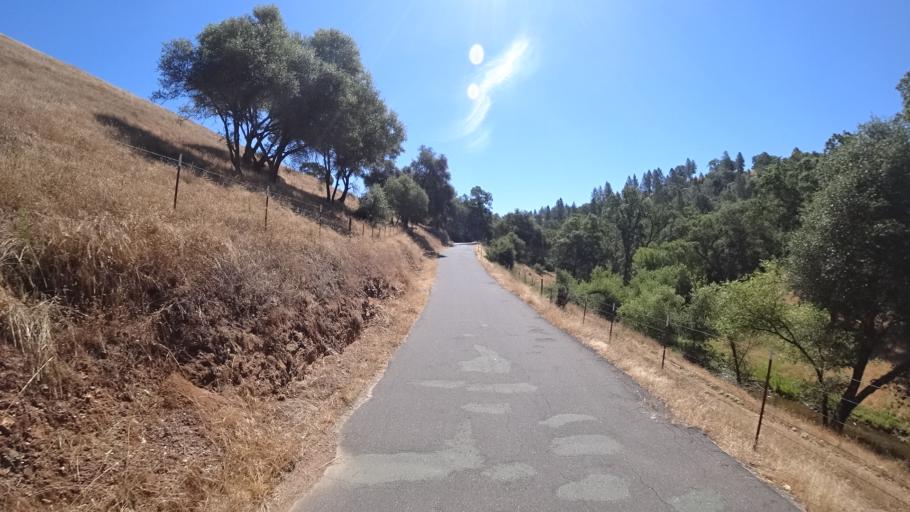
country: US
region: California
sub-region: Calaveras County
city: Angels Camp
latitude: 38.1393
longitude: -120.5527
